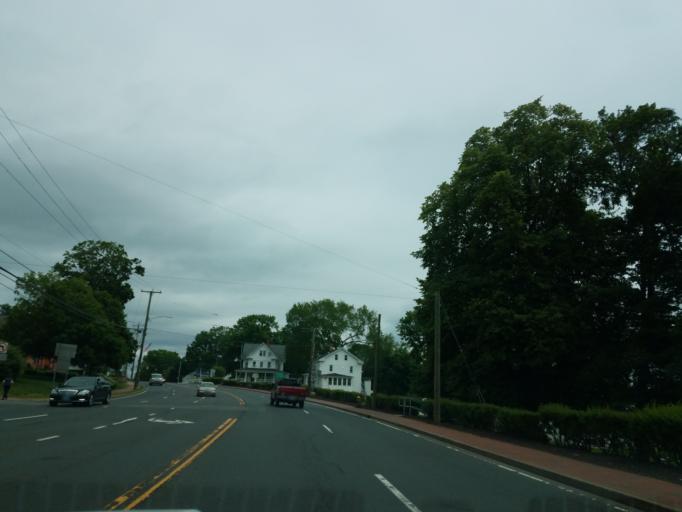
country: US
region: Connecticut
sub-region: New Haven County
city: Cheshire
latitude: 41.4990
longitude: -72.9014
